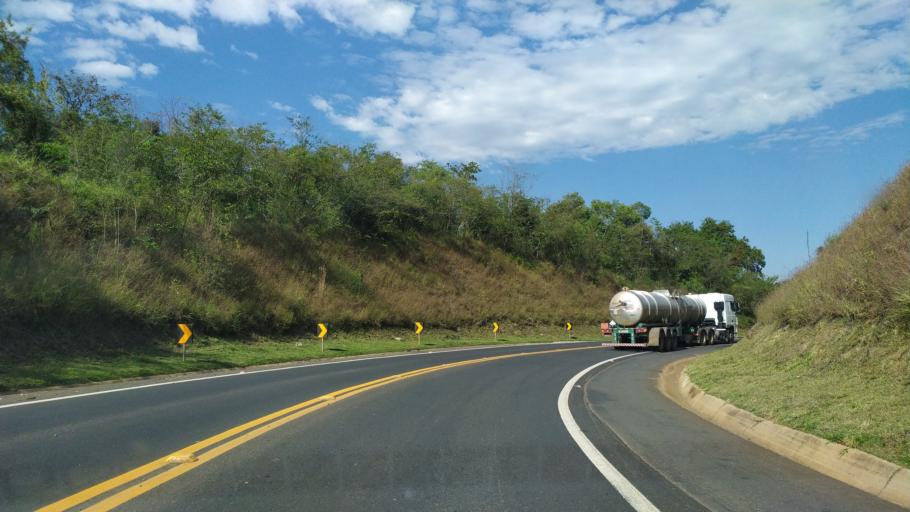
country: BR
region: Parana
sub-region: Telemaco Borba
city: Telemaco Borba
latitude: -24.2723
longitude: -50.7159
